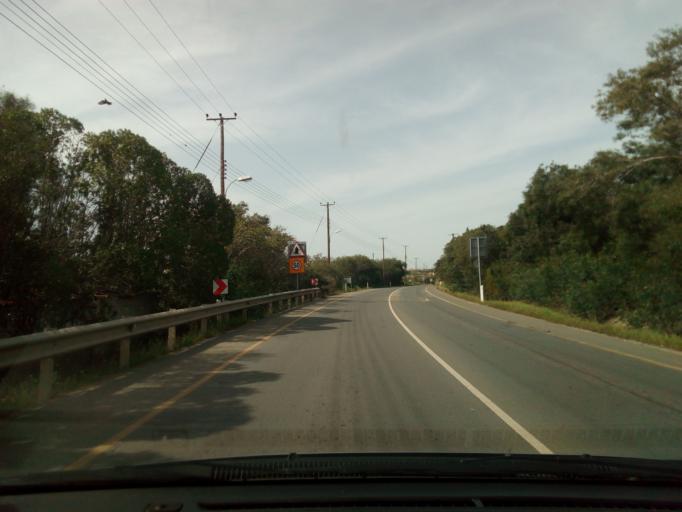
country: CY
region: Lefkosia
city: Arediou
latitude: 35.0522
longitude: 33.2004
